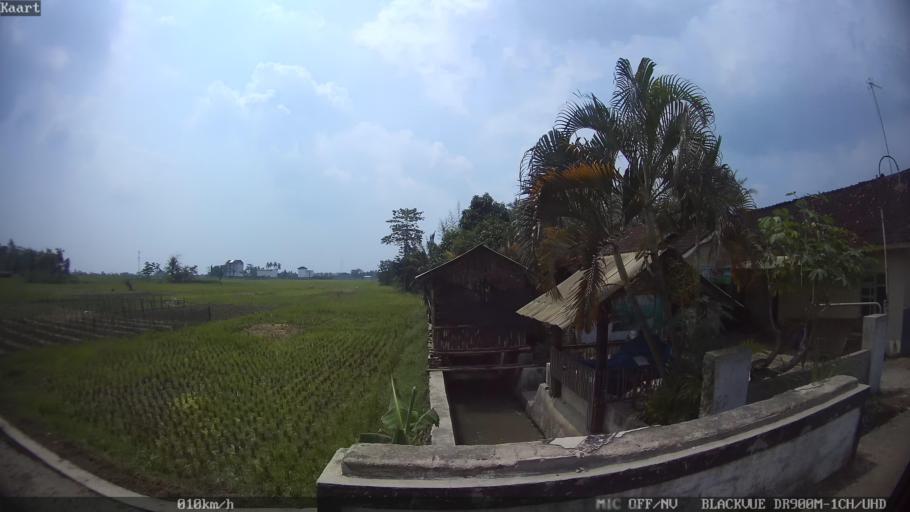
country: ID
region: Lampung
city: Gadingrejo
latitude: -5.3783
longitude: 105.0510
